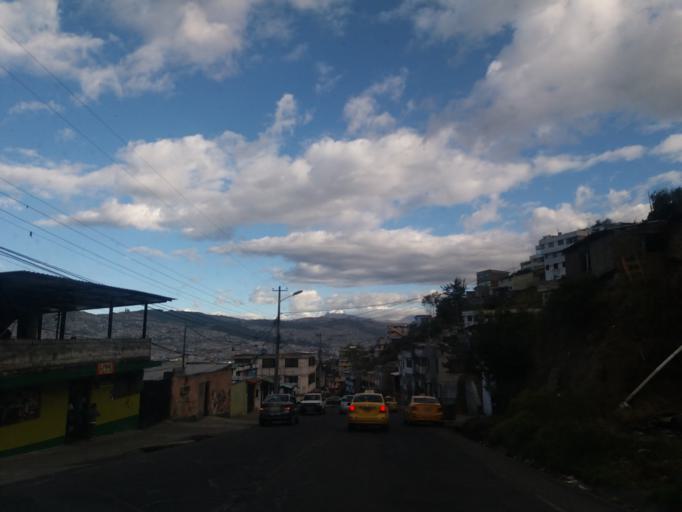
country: EC
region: Pichincha
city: Quito
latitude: -0.2303
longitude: -78.5333
